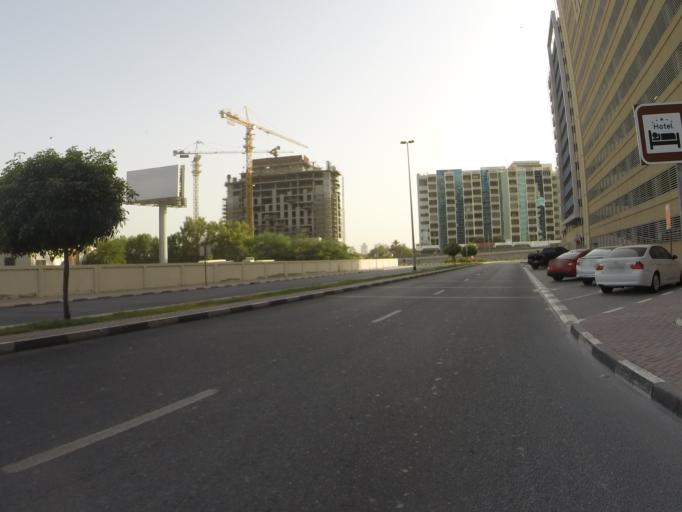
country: AE
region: Ash Shariqah
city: Sharjah
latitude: 25.2302
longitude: 55.2852
